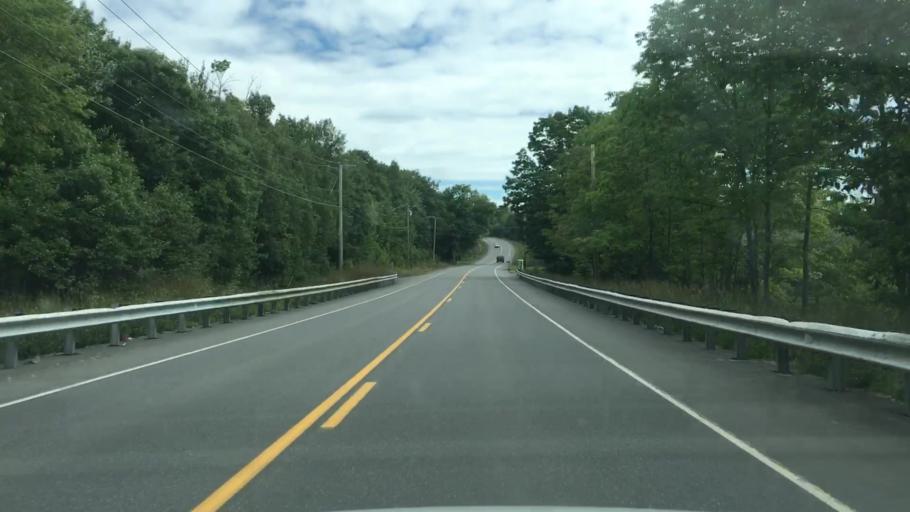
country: US
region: Maine
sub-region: Piscataquis County
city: Milo
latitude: 45.2421
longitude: -69.0261
